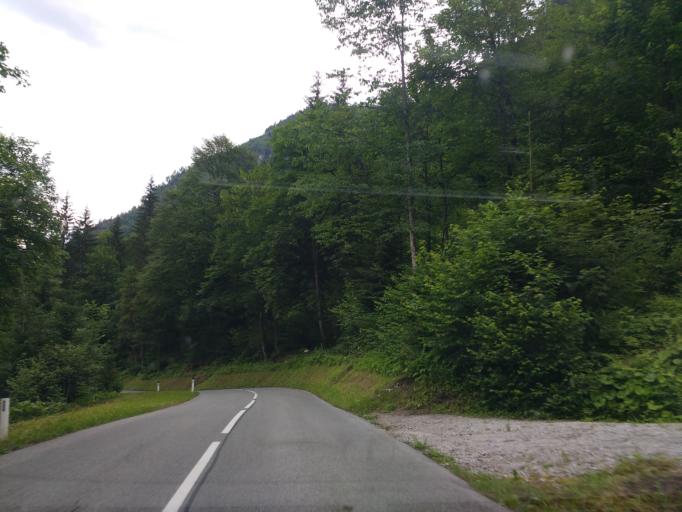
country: AT
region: Salzburg
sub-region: Politischer Bezirk Zell am See
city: Kaprun
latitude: 47.2196
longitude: 12.7282
